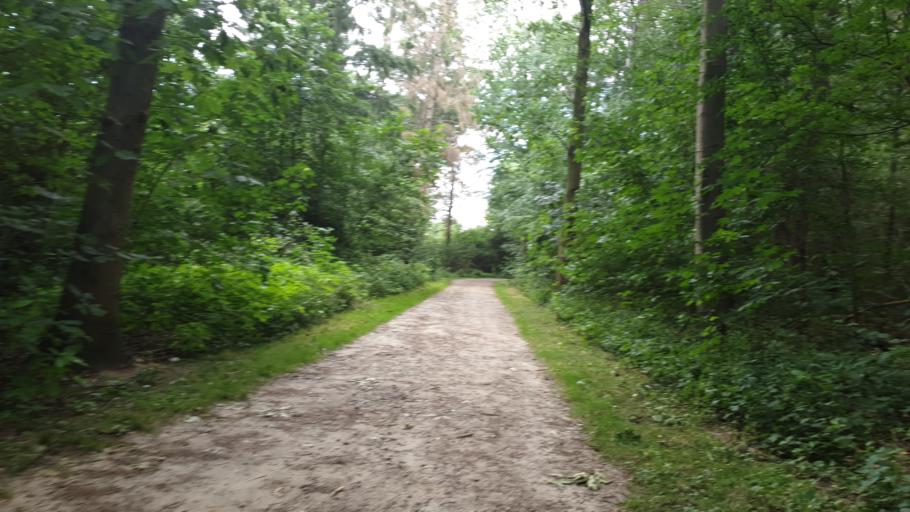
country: DE
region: Hamburg
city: Bergedorf
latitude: 53.4868
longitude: 10.2388
